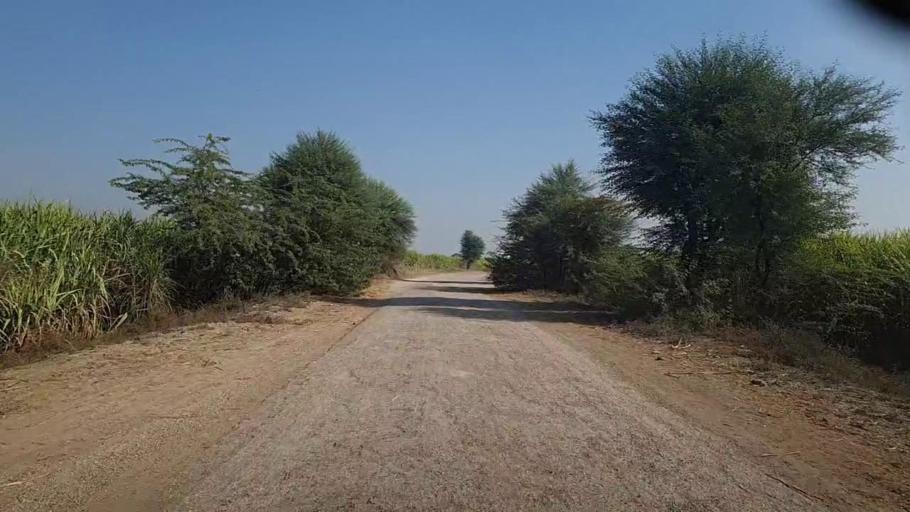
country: PK
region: Sindh
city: Darya Khan Marri
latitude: 26.6698
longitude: 68.3303
